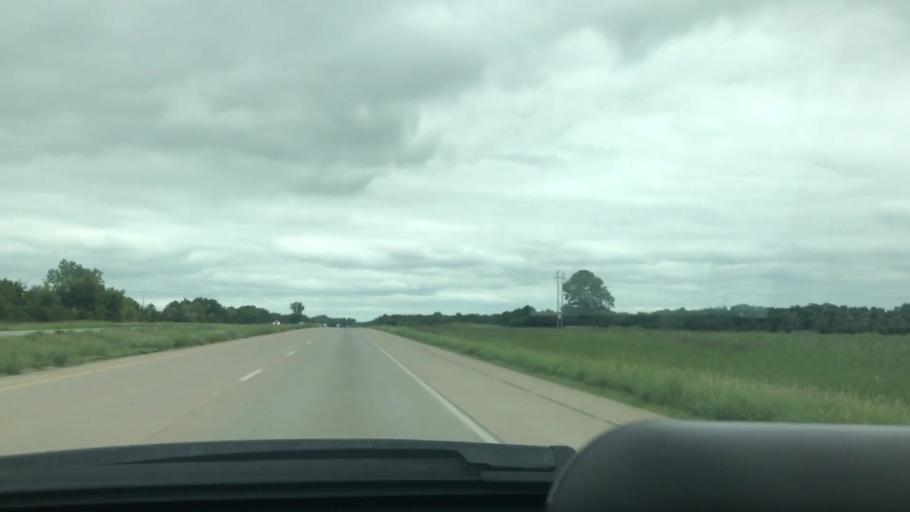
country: US
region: Oklahoma
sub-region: Mayes County
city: Chouteau
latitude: 36.2114
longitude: -95.3408
